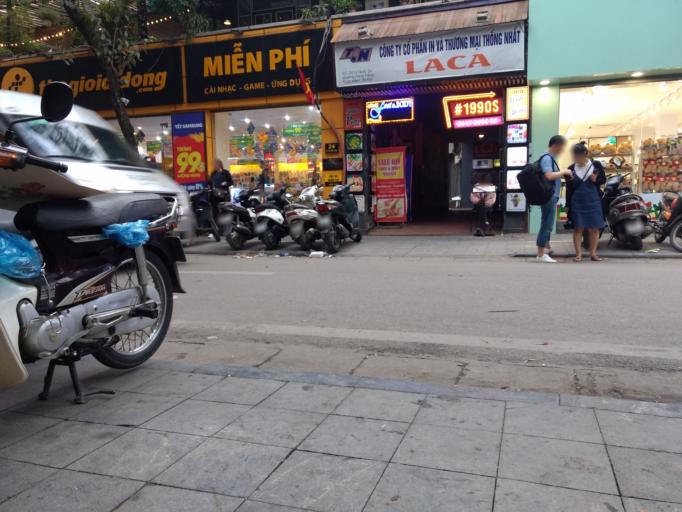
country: VN
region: Ha Noi
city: Hoan Kiem
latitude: 21.0300
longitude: 105.8492
